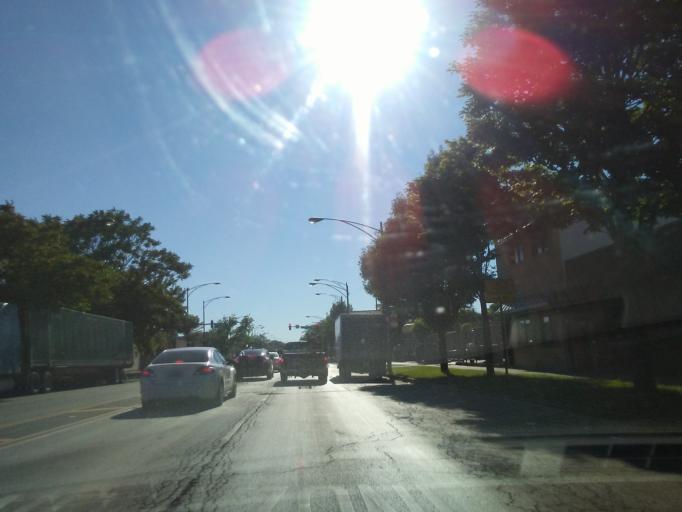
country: US
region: Illinois
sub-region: Cook County
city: Oak Park
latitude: 41.9243
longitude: -87.7428
